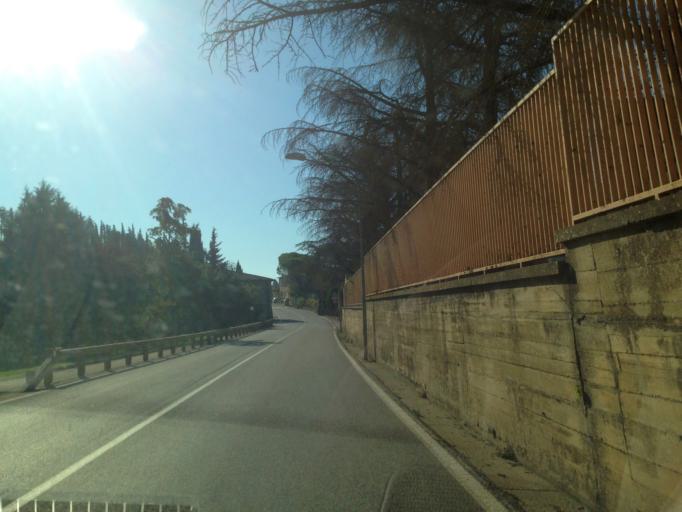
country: IT
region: Tuscany
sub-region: Provincia di Siena
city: Castellina in Chianti
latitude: 43.4628
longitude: 11.2900
